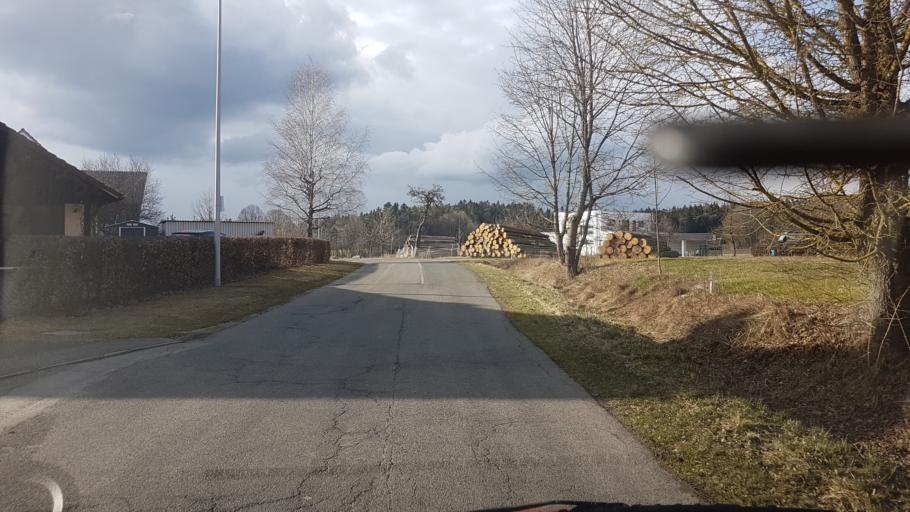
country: DE
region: Bavaria
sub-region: Upper Franconia
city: Stadelhofen
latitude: 50.0045
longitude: 11.1748
